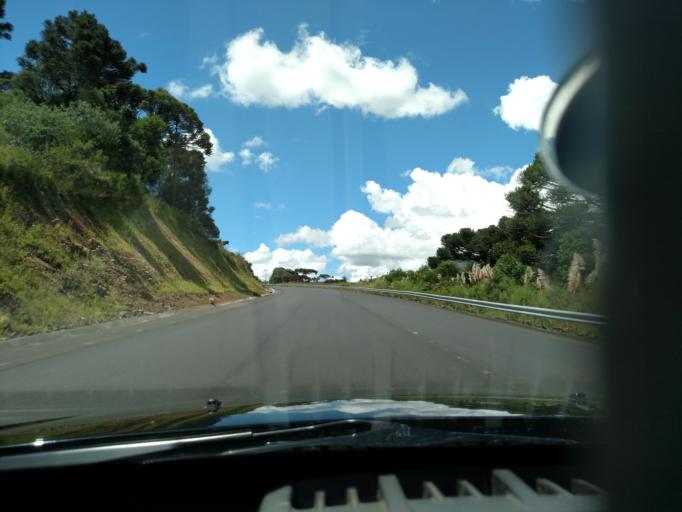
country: BR
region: Santa Catarina
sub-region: Sao Joaquim
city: Sao Joaquim
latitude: -28.2470
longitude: -49.9713
